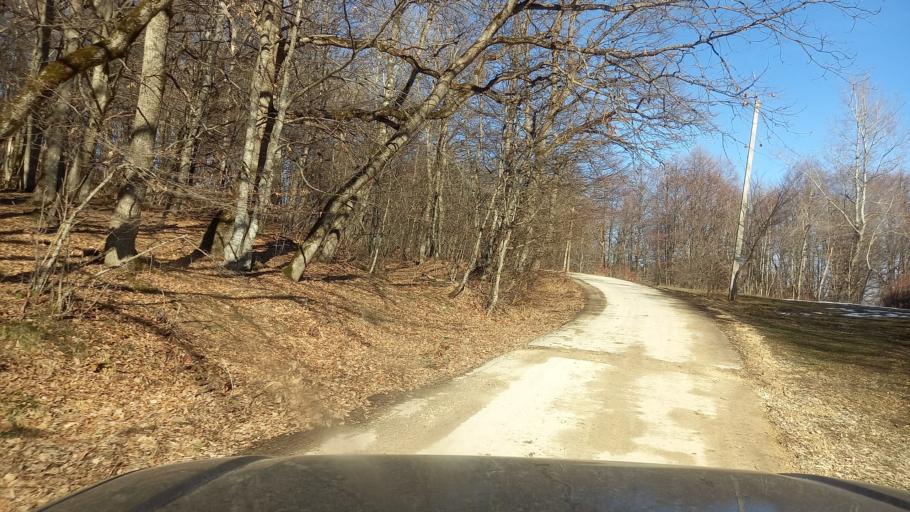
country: RU
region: Adygeya
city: Kamennomostskiy
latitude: 44.2841
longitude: 40.3169
